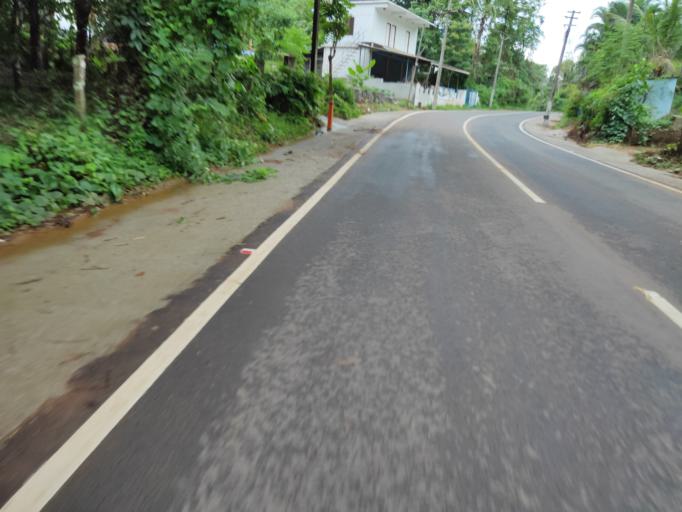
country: IN
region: Kerala
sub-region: Malappuram
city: Manjeri
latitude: 11.1861
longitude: 76.2099
